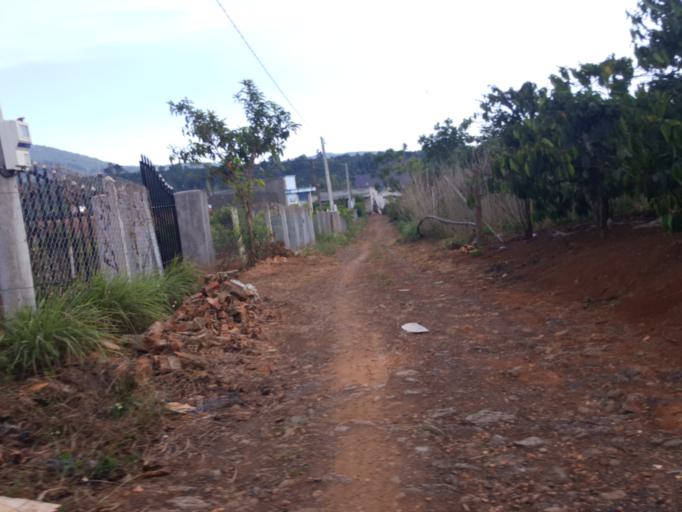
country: VN
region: Lam Dong
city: Duc Trong
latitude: 11.8369
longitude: 108.3486
